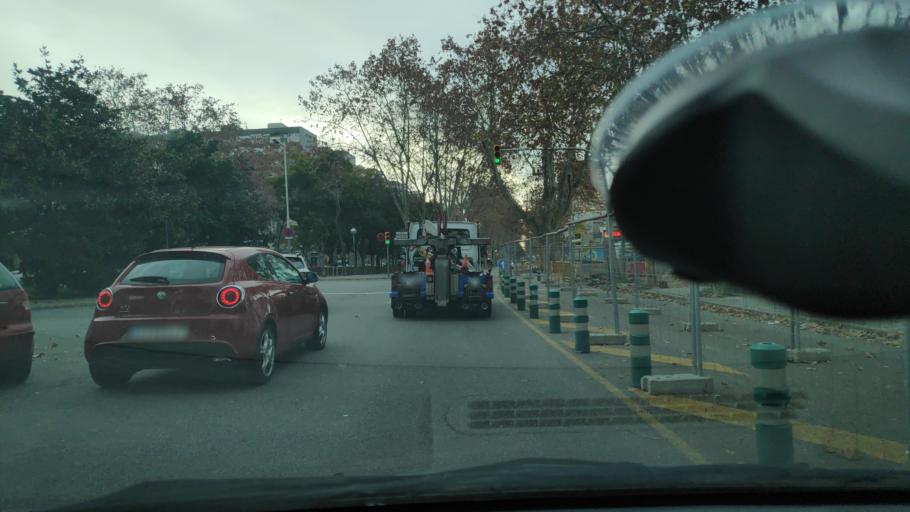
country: ES
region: Catalonia
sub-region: Provincia de Barcelona
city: Sant Marti
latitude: 41.4185
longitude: 2.2093
